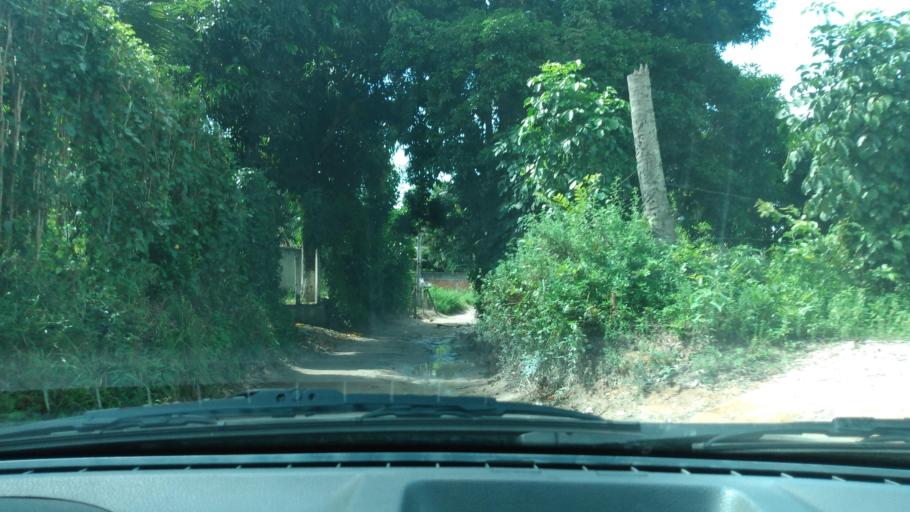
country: BR
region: Pernambuco
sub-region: Cabo De Santo Agostinho
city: Cabo
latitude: -8.3541
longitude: -34.9655
